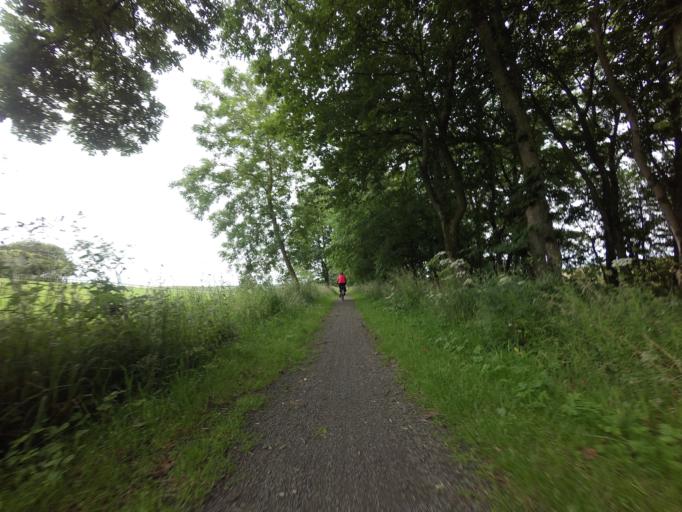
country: GB
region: Scotland
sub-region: Aberdeenshire
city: Ellon
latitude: 57.4753
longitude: -2.1273
